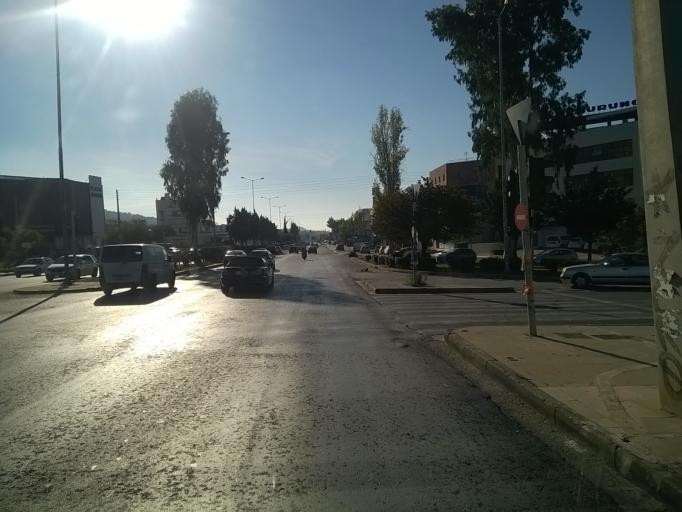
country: GR
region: Attica
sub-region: Nomarchia Athinas
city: Glyfada
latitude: 37.8753
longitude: 23.7566
